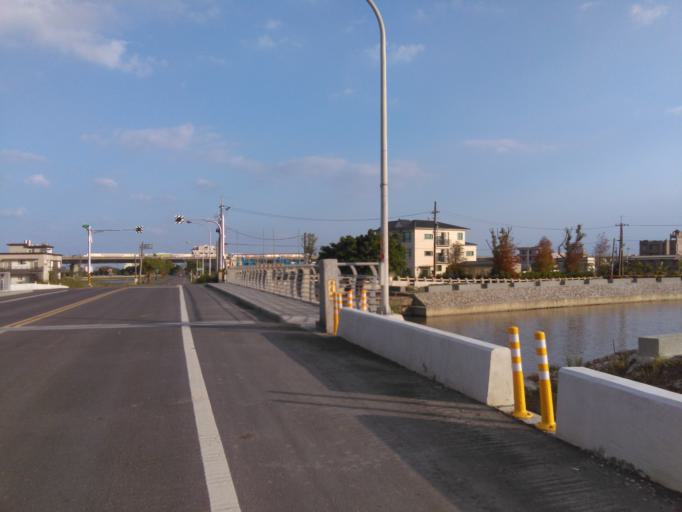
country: TW
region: Taiwan
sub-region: Yilan
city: Yilan
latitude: 24.8026
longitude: 121.7793
